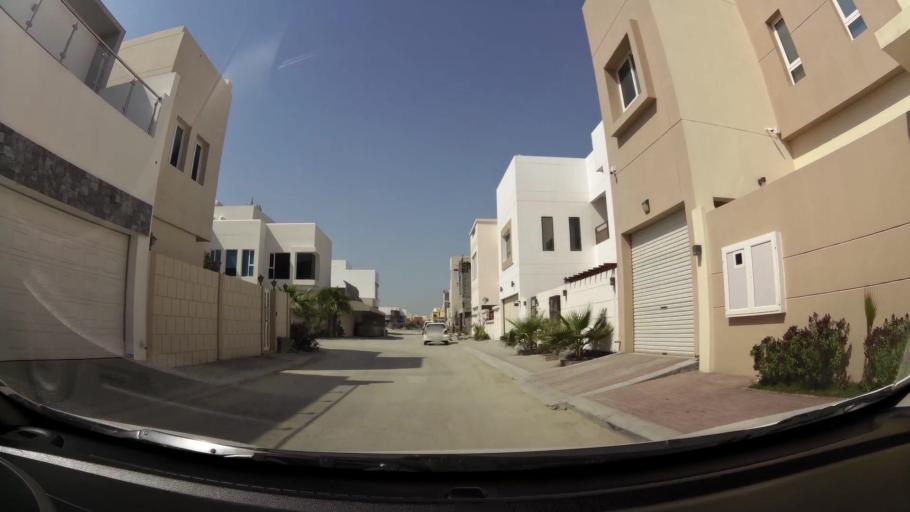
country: BH
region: Manama
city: Jidd Hafs
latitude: 26.2058
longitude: 50.4675
